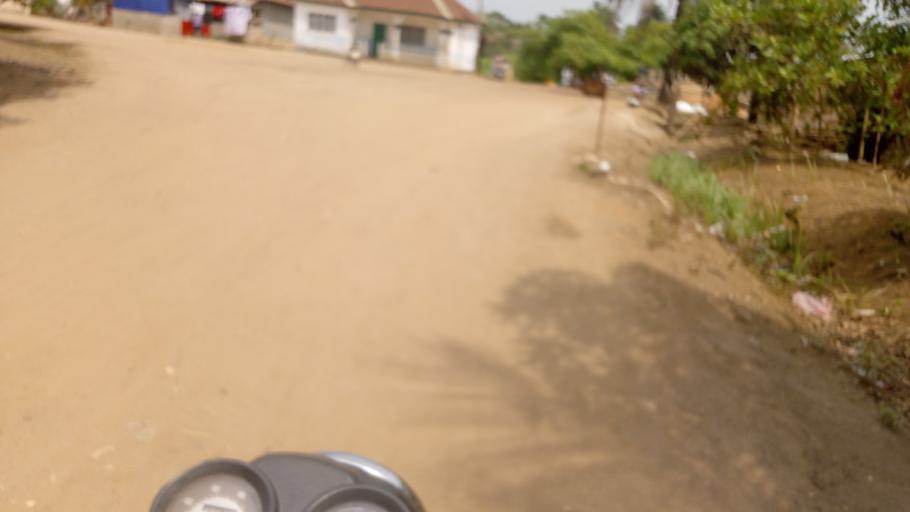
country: SL
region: Western Area
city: Waterloo
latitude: 8.3090
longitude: -13.0655
